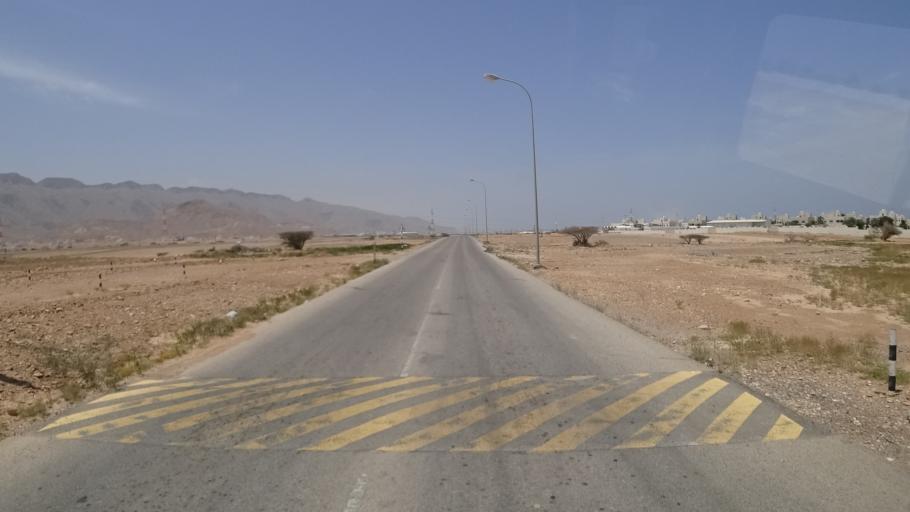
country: OM
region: Ash Sharqiyah
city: Sur
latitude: 22.6029
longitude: 59.4372
